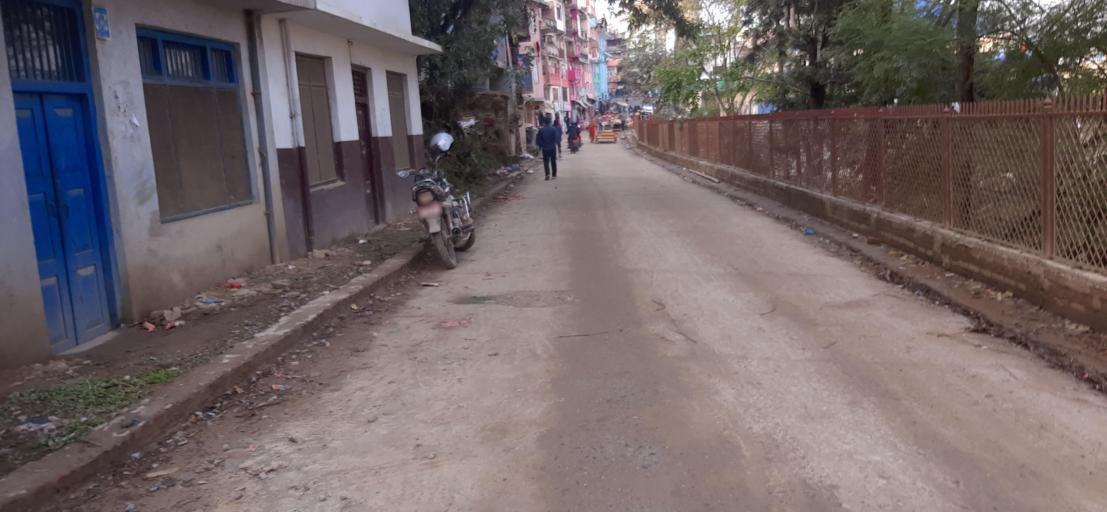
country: NP
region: Central Region
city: Kirtipur
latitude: 27.6754
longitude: 85.2816
